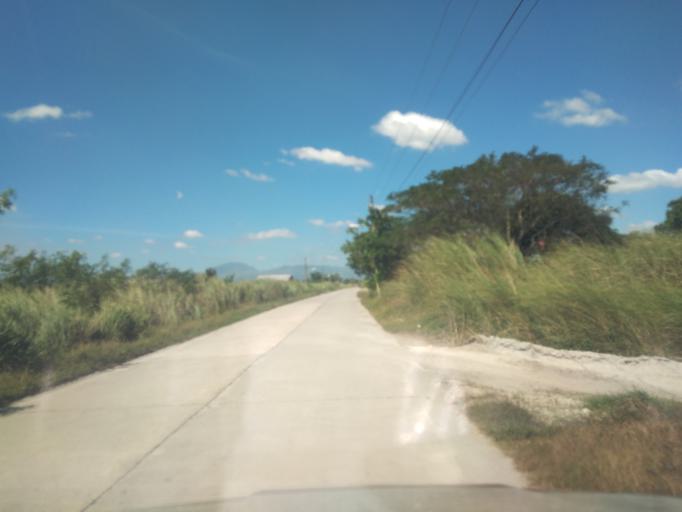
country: PH
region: Central Luzon
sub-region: Province of Pampanga
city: Balas
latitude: 15.0525
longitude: 120.6083
